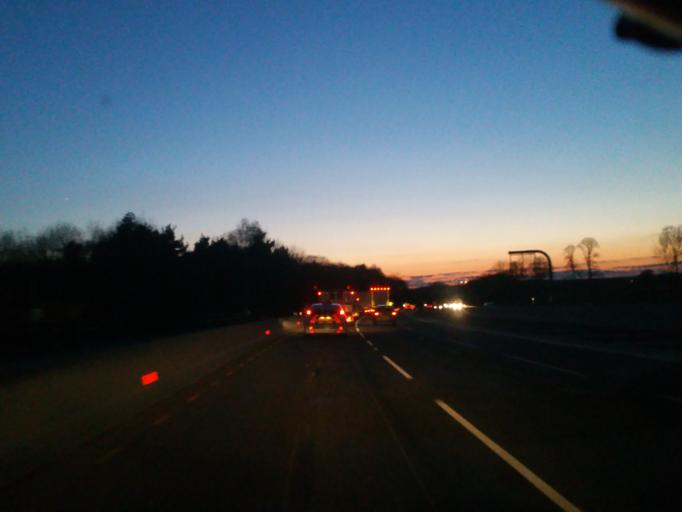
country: GB
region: England
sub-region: Surrey
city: Windlesham
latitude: 51.3584
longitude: -0.6580
